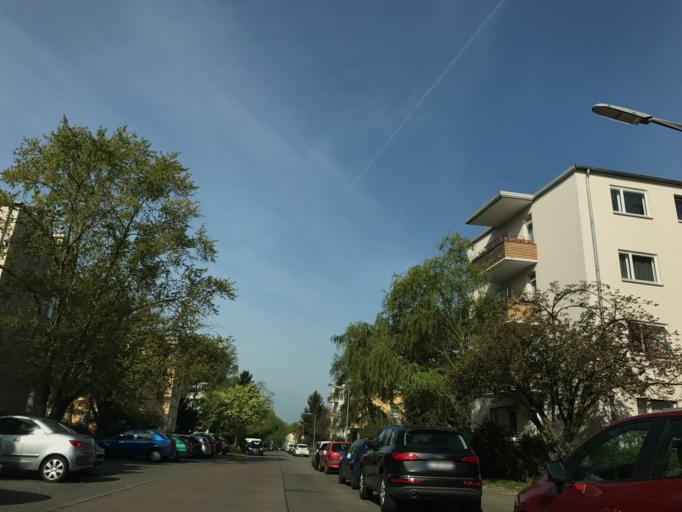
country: DE
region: Berlin
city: Staaken
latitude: 52.5338
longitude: 13.1526
